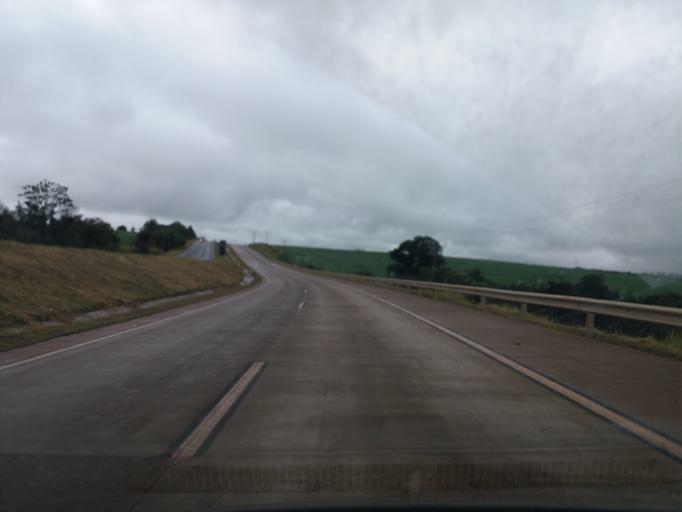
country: BR
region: Parana
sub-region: Cascavel
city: Cascavel
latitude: -25.0459
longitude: -53.5563
